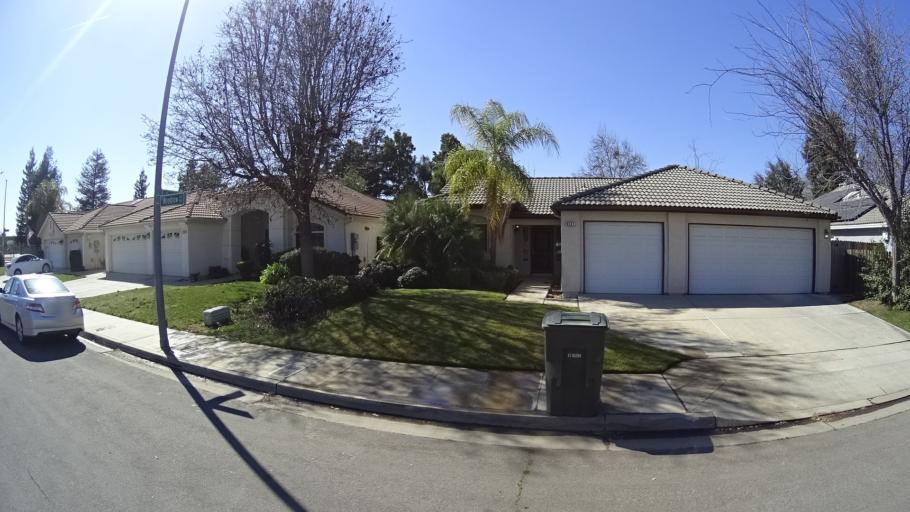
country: US
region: California
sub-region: Fresno County
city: Clovis
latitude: 36.8599
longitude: -119.7451
